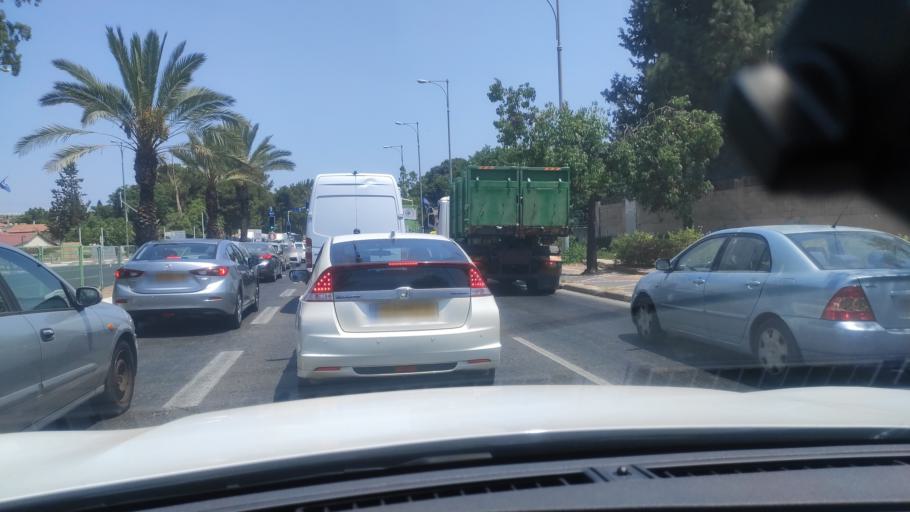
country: IL
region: Central District
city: Petah Tiqwa
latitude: 32.0873
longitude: 34.9015
